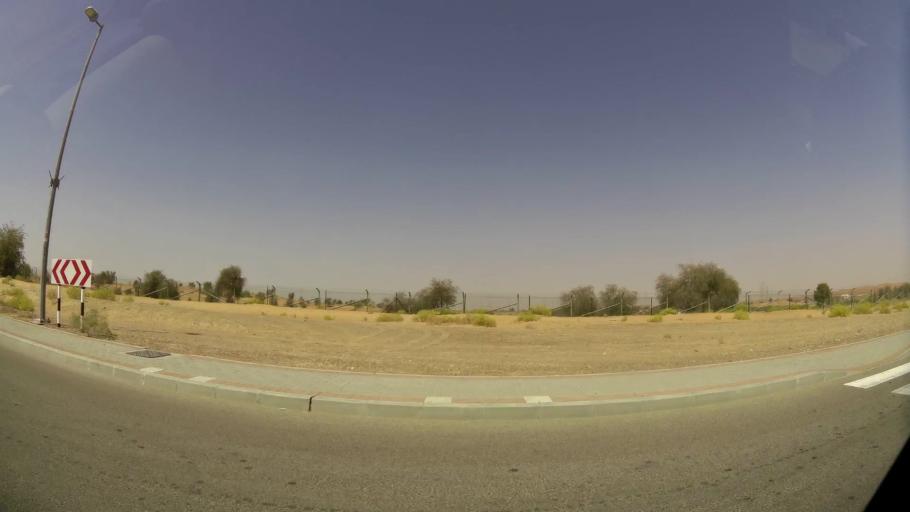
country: OM
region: Al Buraimi
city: Al Buraymi
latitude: 24.3016
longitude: 55.7487
